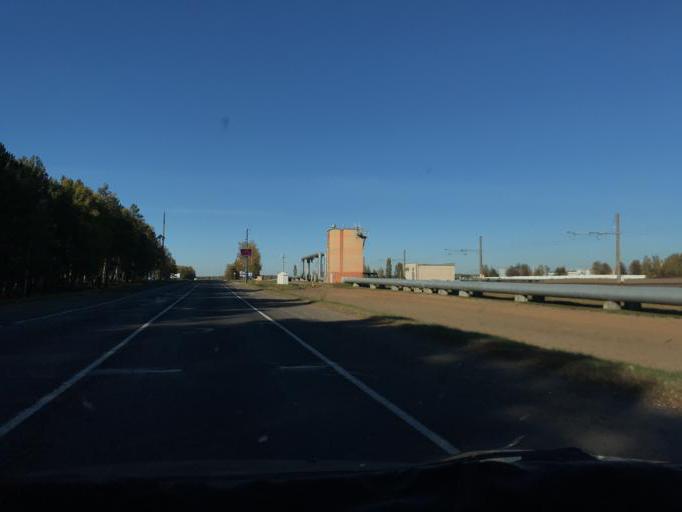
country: BY
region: Gomel
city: Mazyr
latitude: 51.9950
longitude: 29.2585
